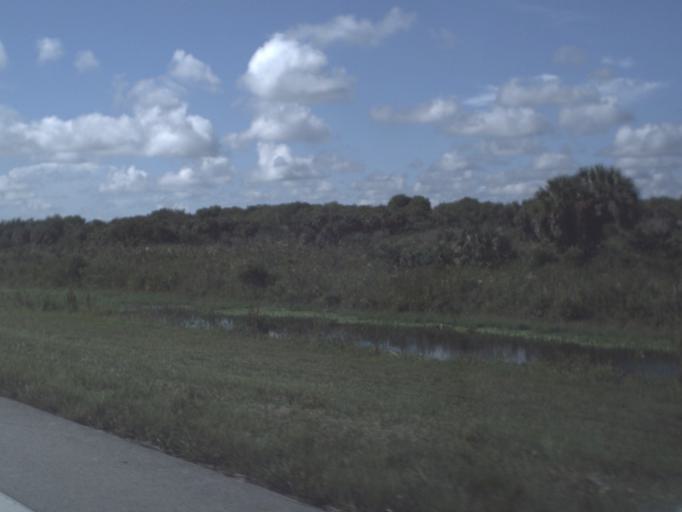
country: US
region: Florida
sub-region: Glades County
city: Moore Haven
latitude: 26.9306
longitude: -81.1223
